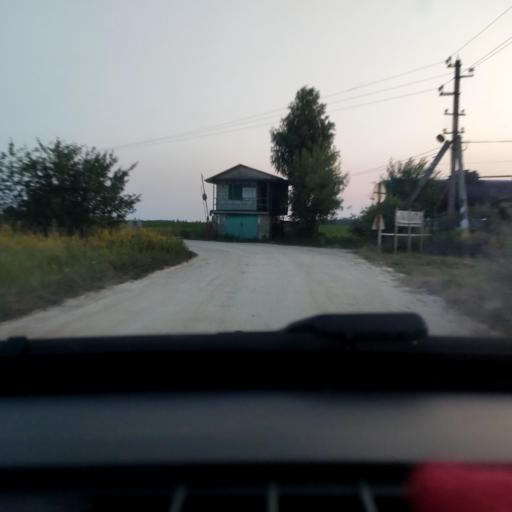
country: RU
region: Voronezj
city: Podgornoye
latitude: 51.8615
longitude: 39.1064
